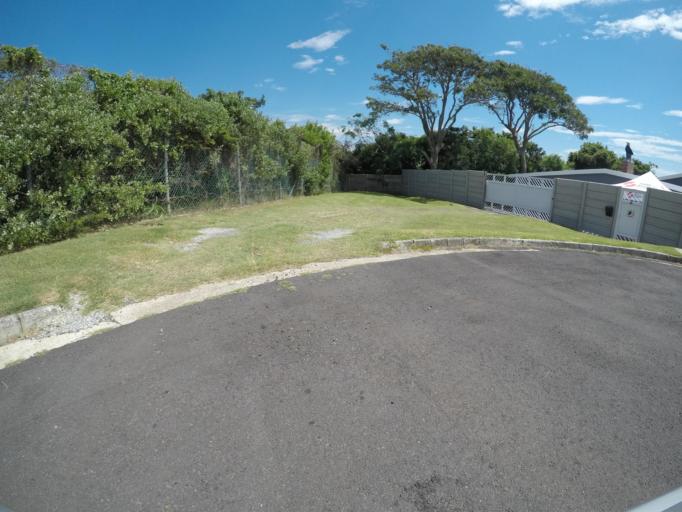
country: ZA
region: Eastern Cape
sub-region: Buffalo City Metropolitan Municipality
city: East London
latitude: -33.0370
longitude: 27.8847
